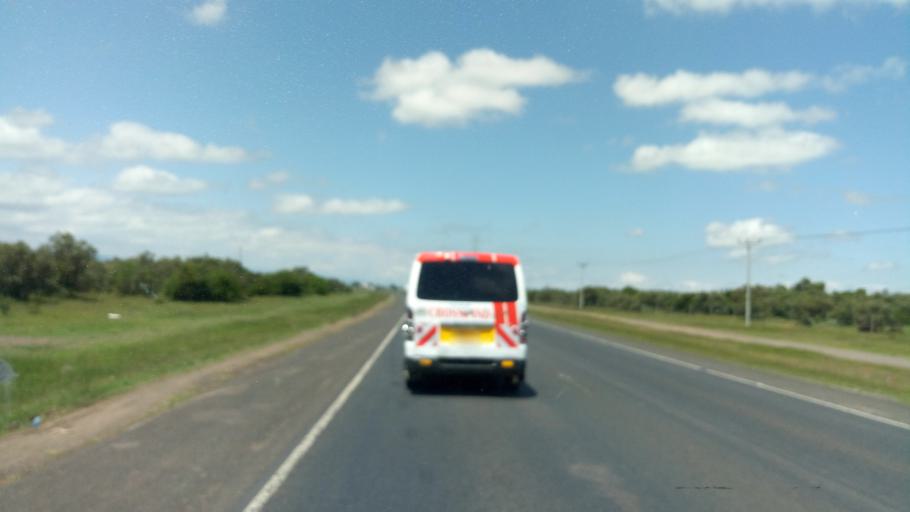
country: KE
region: Nakuru
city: Naivasha
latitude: -0.5347
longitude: 36.3335
